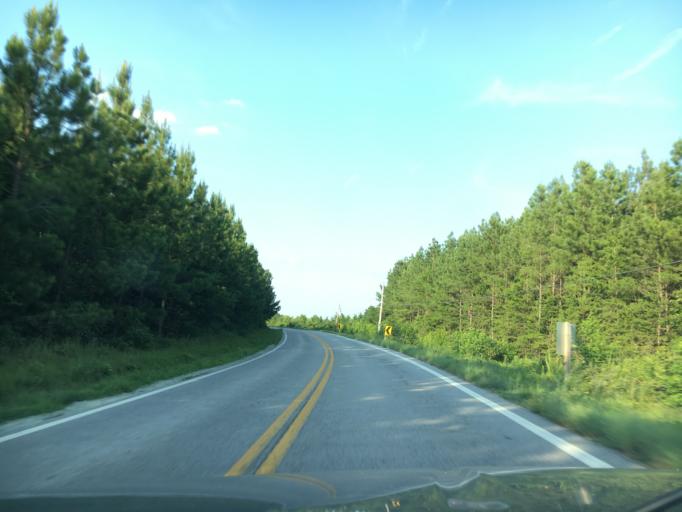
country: US
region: Virginia
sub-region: Pittsylvania County
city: Chatham
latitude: 36.8179
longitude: -79.3357
